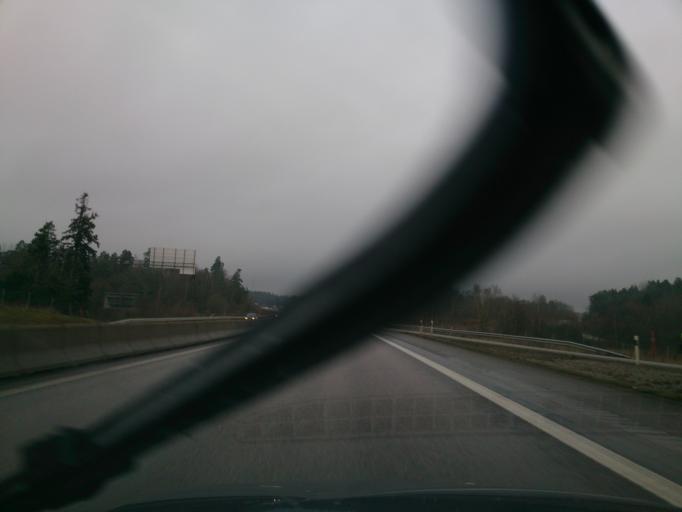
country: SE
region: OEstergoetland
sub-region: Norrkopings Kommun
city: Kimstad
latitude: 58.5530
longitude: 16.0555
